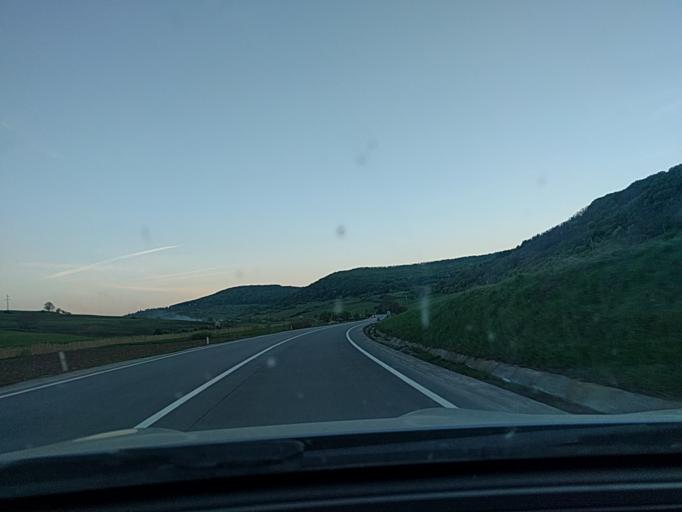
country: RO
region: Mures
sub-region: Comuna Nades
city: Nades
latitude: 46.3111
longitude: 24.7228
